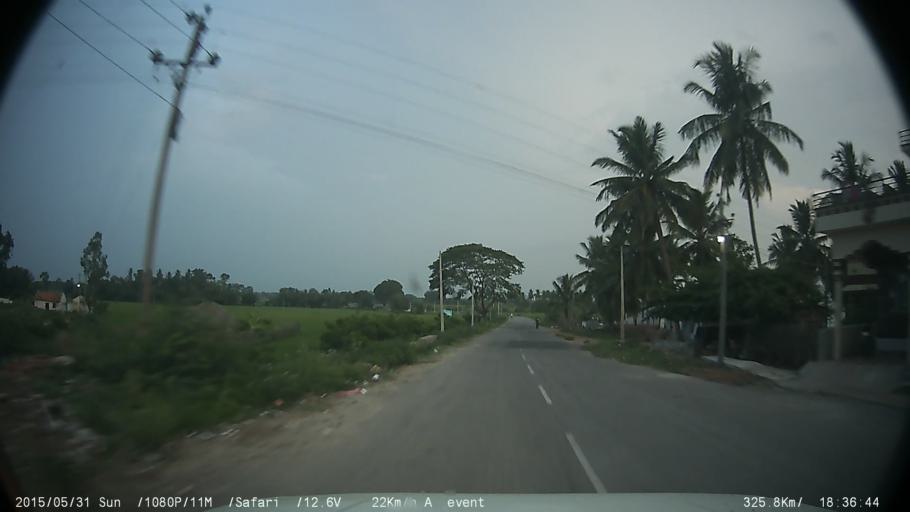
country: IN
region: Karnataka
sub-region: Mysore
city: Nanjangud
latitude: 12.1463
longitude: 76.7663
